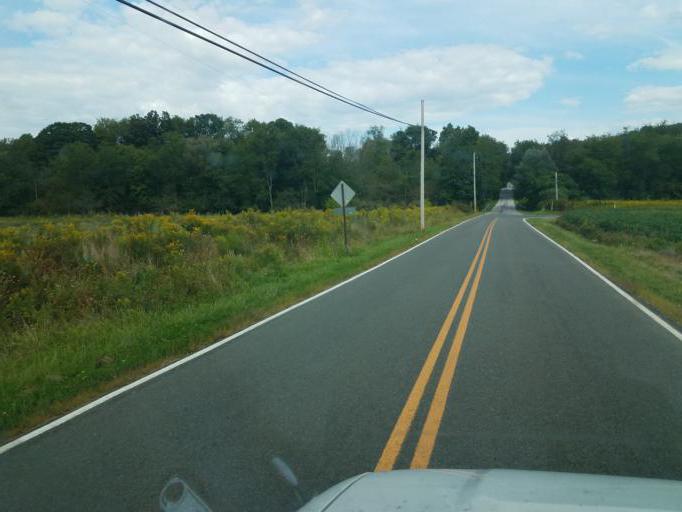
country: US
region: Ohio
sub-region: Stark County
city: East Canton
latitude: 40.7324
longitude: -81.2787
